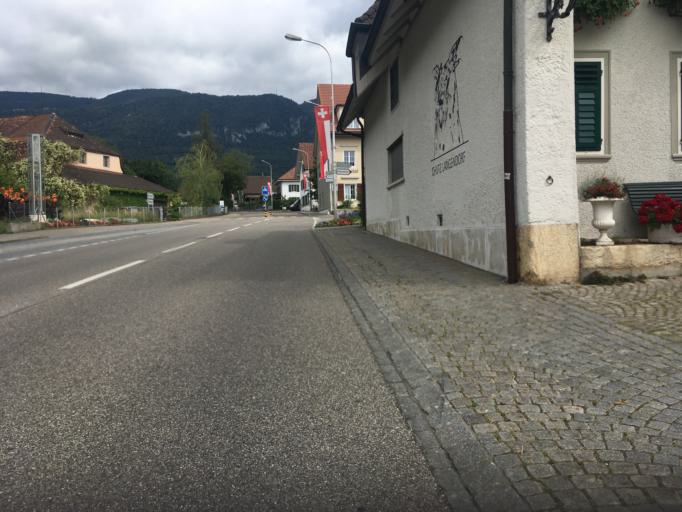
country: CH
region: Solothurn
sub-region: Bezirk Lebern
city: Langendorf
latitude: 47.2213
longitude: 7.5150
